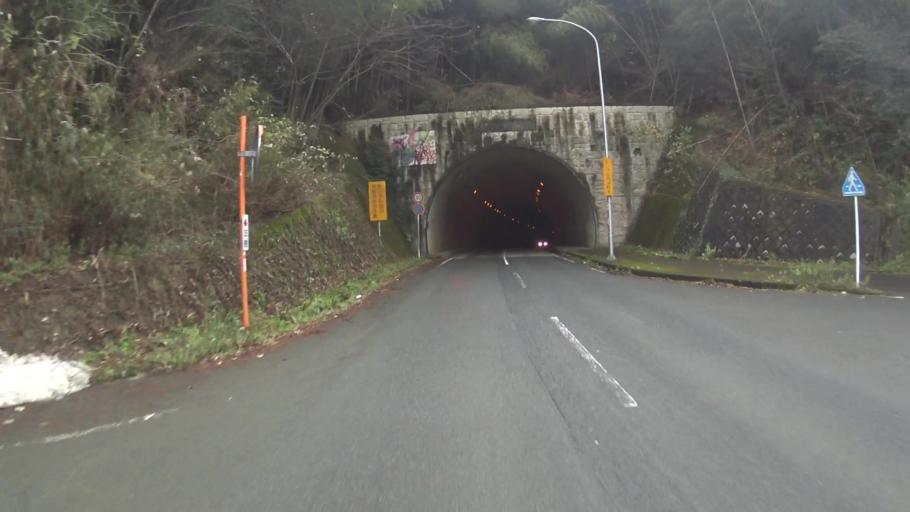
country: JP
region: Kyoto
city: Maizuru
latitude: 35.4759
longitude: 135.3162
